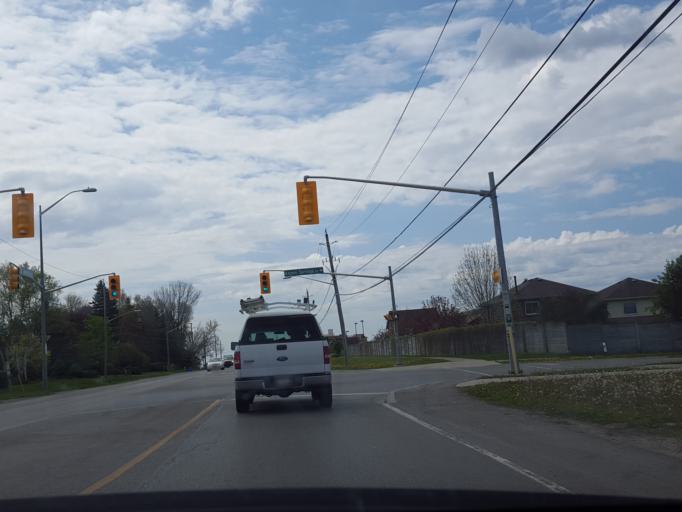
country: CA
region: Ontario
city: Oshawa
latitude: 43.9073
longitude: -78.7005
